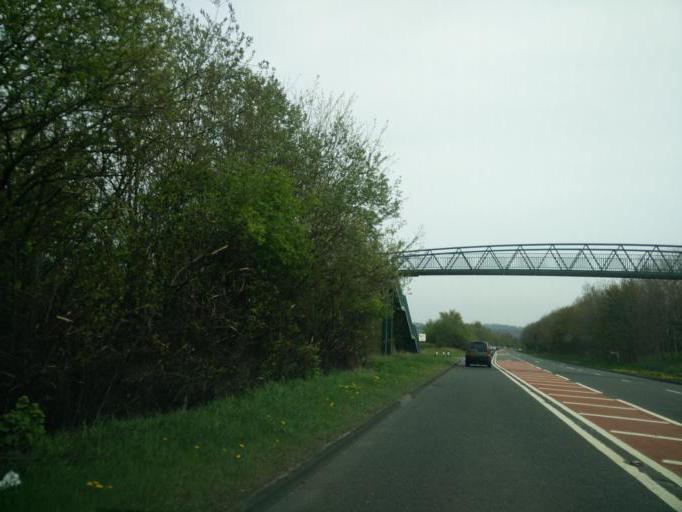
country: GB
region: England
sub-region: County Durham
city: Bishop Auckland
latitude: 54.6723
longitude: -1.6916
